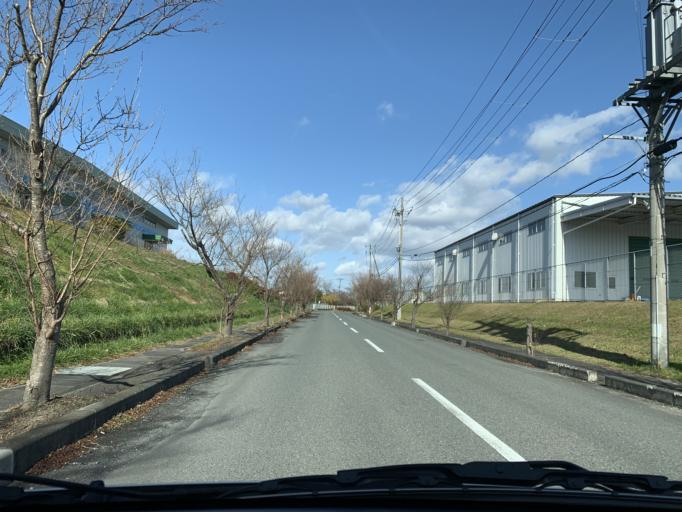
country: JP
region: Iwate
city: Mizusawa
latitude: 39.0302
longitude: 141.1133
